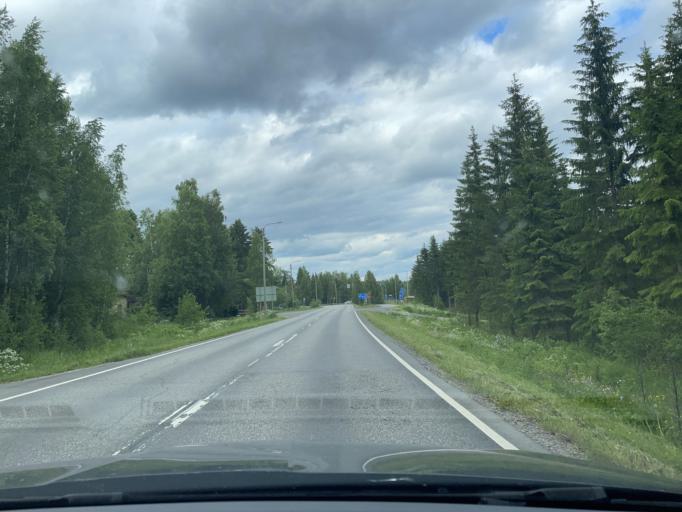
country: FI
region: Central Finland
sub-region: Jyvaeskylae
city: Petaejaevesi
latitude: 62.2459
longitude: 25.1693
